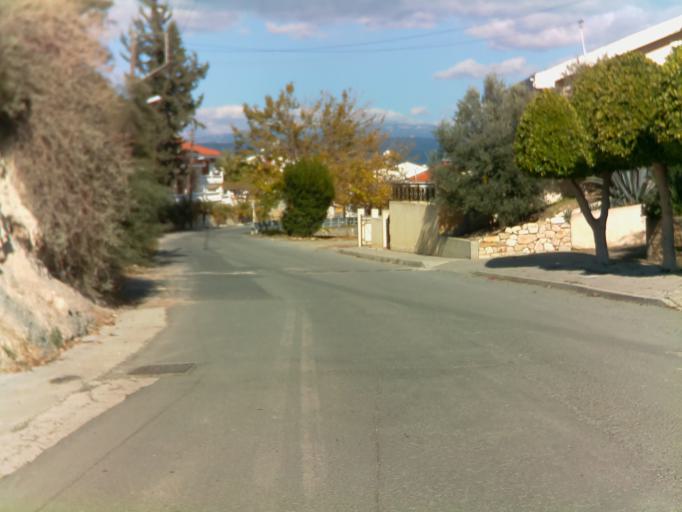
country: CY
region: Limassol
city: Pissouri
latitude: 34.6674
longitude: 32.6987
